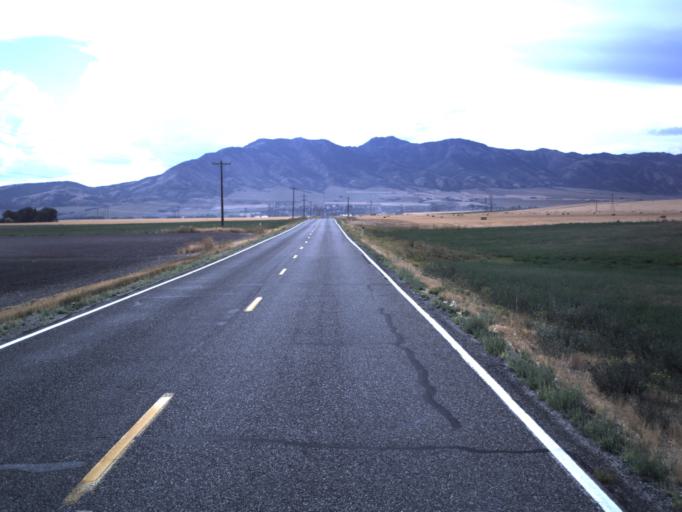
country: US
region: Utah
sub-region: Cache County
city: Lewiston
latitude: 41.9175
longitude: -111.9803
